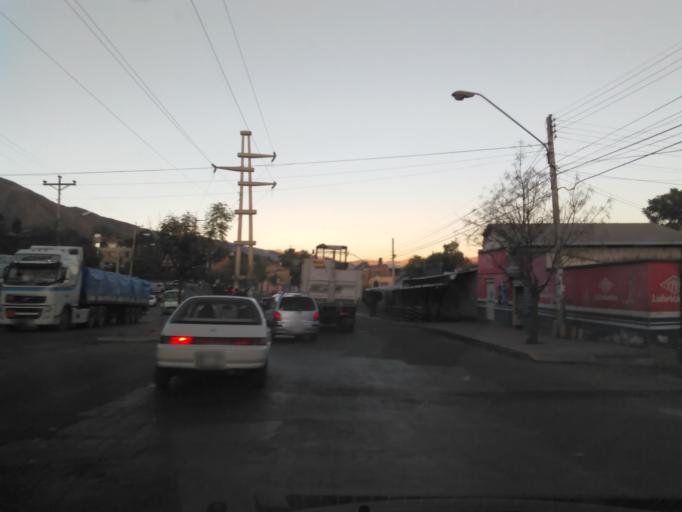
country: BO
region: Cochabamba
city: Cochabamba
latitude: -17.3728
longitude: -66.1363
